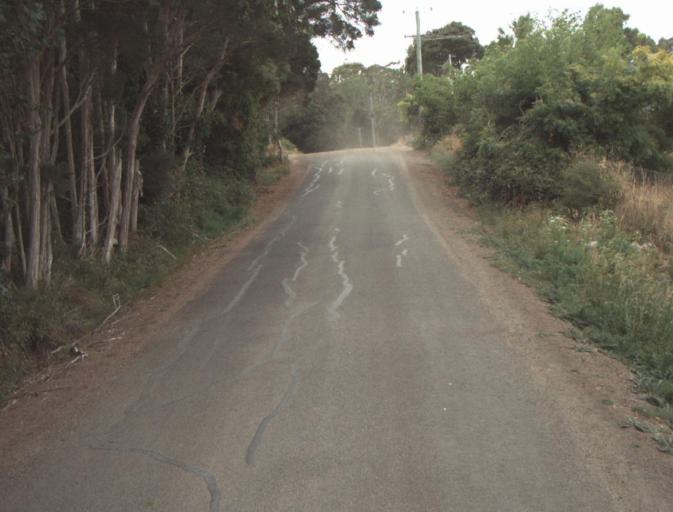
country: AU
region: Tasmania
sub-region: Launceston
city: Mayfield
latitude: -41.2727
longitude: 147.1832
